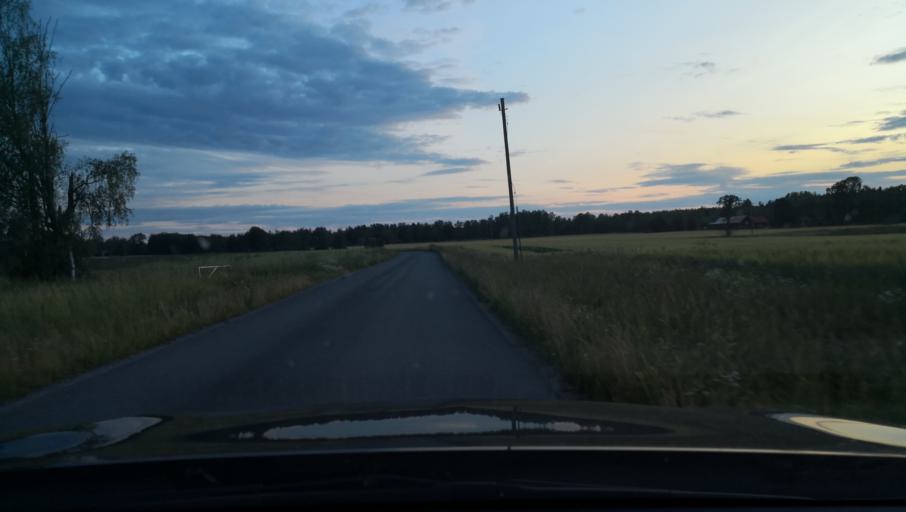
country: SE
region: Uppsala
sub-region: Osthammars Kommun
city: Bjorklinge
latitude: 60.0357
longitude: 17.4787
